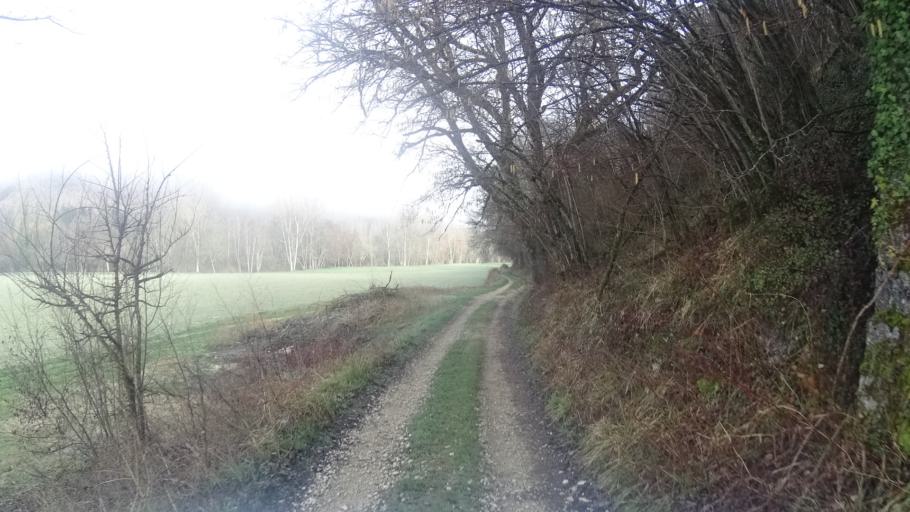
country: FR
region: Aquitaine
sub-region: Departement de la Dordogne
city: Terrasson-Lavilledieu
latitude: 45.0930
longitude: 1.2639
